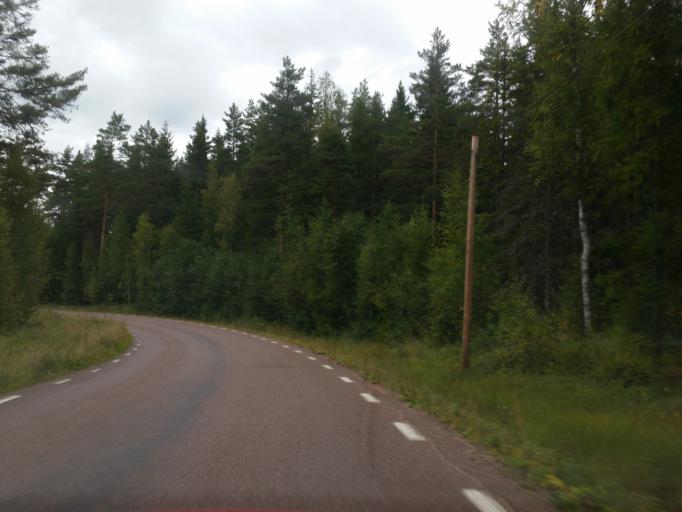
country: SE
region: Dalarna
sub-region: Gagnefs Kommun
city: Gagnef
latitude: 60.6741
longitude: 15.1721
